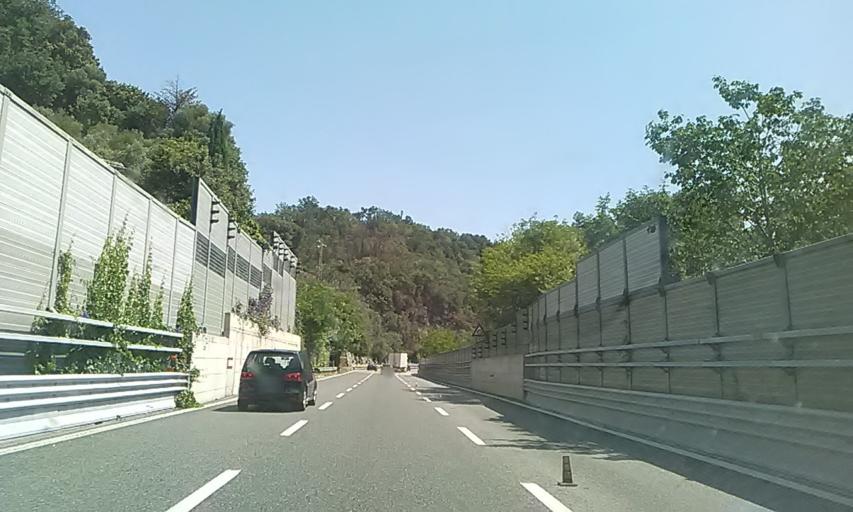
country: IT
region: Liguria
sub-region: Provincia di Genova
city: Cogoleto
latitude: 44.3914
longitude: 8.6402
